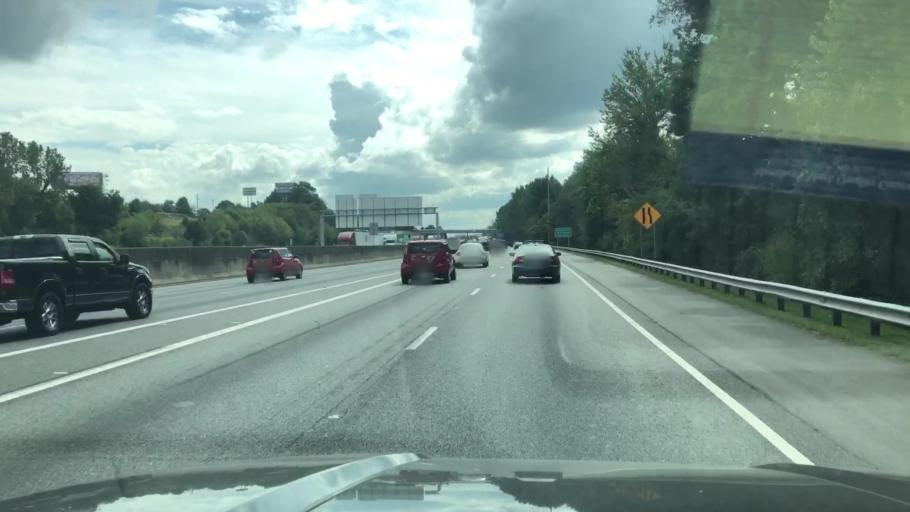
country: US
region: Georgia
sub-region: Clayton County
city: Forest Park
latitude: 33.6231
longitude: -84.4001
